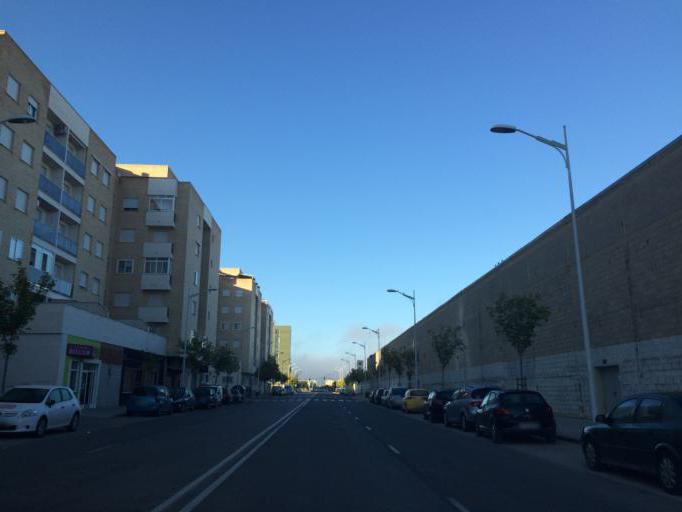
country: ES
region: Castille-La Mancha
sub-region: Provincia de Albacete
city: Albacete
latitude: 39.0088
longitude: -1.8725
